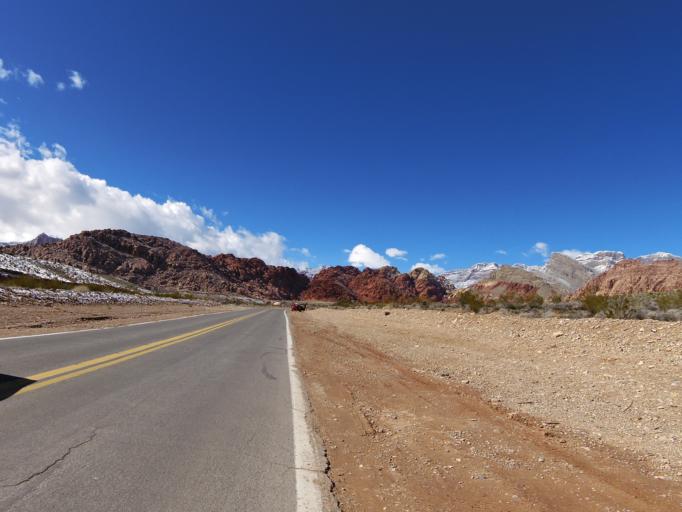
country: US
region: Nevada
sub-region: Clark County
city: Summerlin South
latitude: 36.1463
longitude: -115.4055
